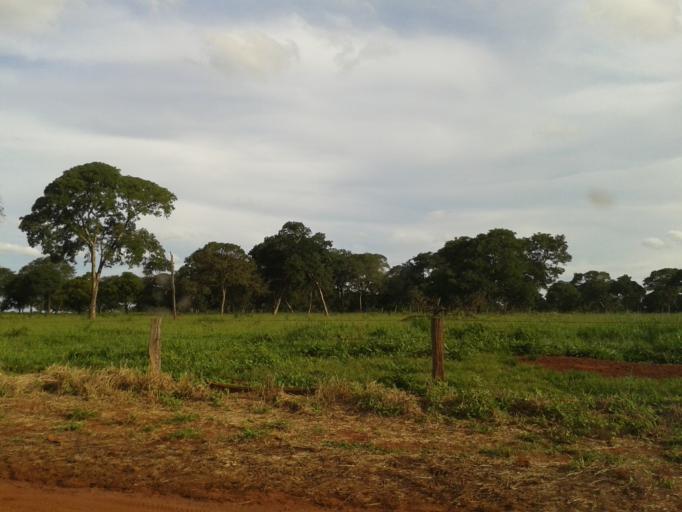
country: BR
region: Minas Gerais
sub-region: Capinopolis
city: Capinopolis
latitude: -18.7937
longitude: -49.8107
